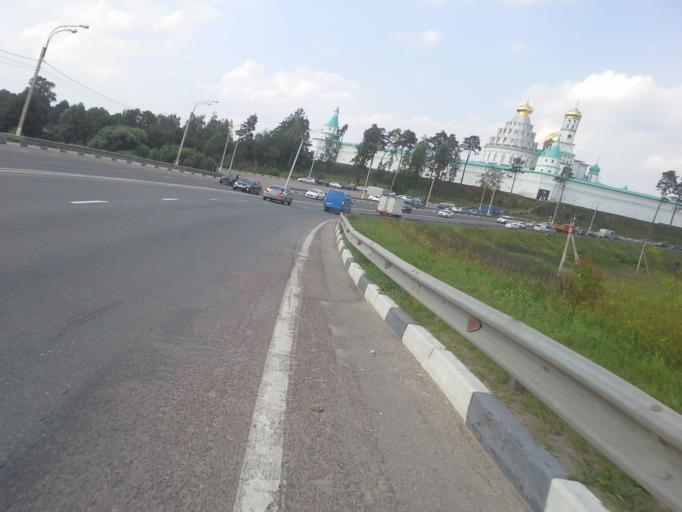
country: RU
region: Moskovskaya
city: Istra
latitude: 55.9182
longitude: 36.8432
